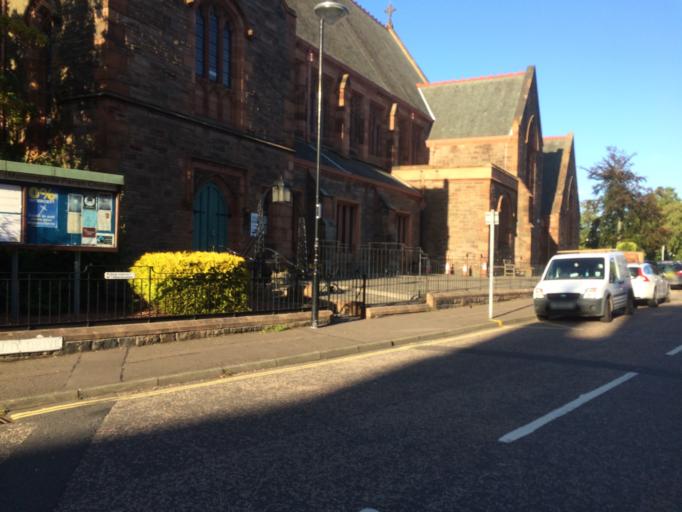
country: GB
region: Scotland
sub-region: Edinburgh
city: Edinburgh
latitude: 55.9233
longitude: -3.2092
